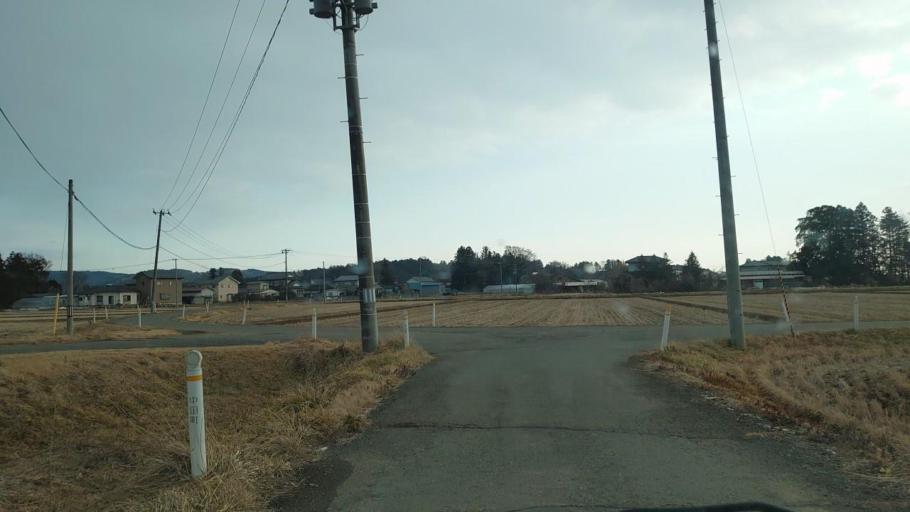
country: JP
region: Miyagi
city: Wakuya
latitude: 38.7037
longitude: 141.2641
